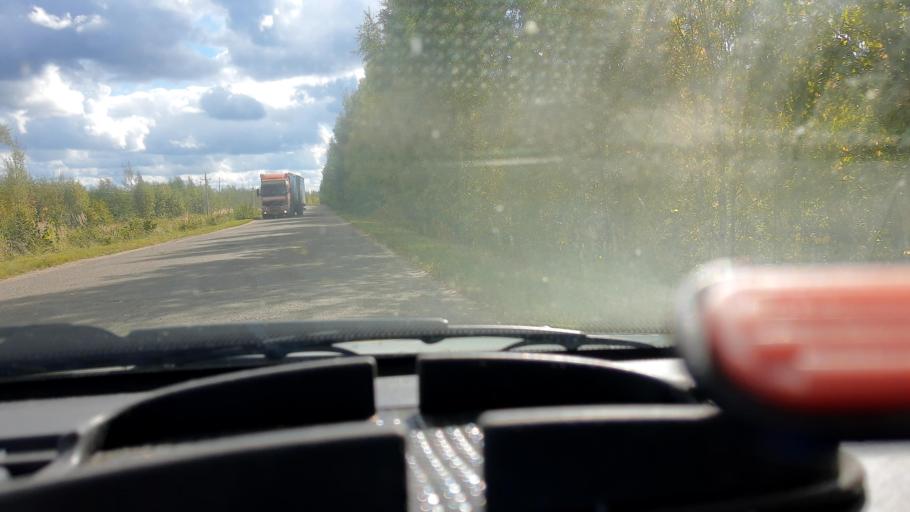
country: RU
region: Mariy-El
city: Kilemary
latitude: 56.8885
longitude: 46.7591
